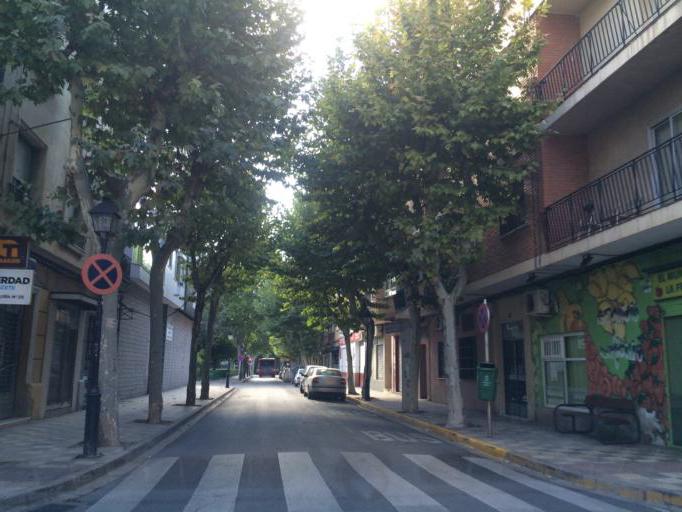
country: ES
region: Castille-La Mancha
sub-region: Provincia de Albacete
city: Albacete
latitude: 38.9937
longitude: -1.8654
